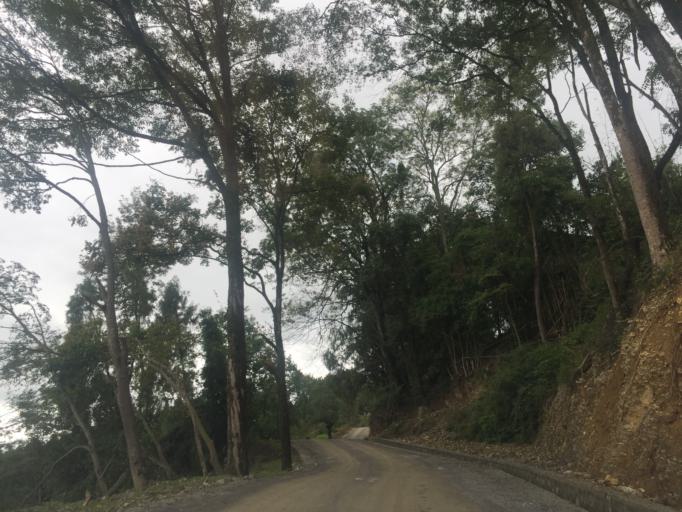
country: CN
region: Guizhou Sheng
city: Shiqian
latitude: 27.6798
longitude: 108.1156
